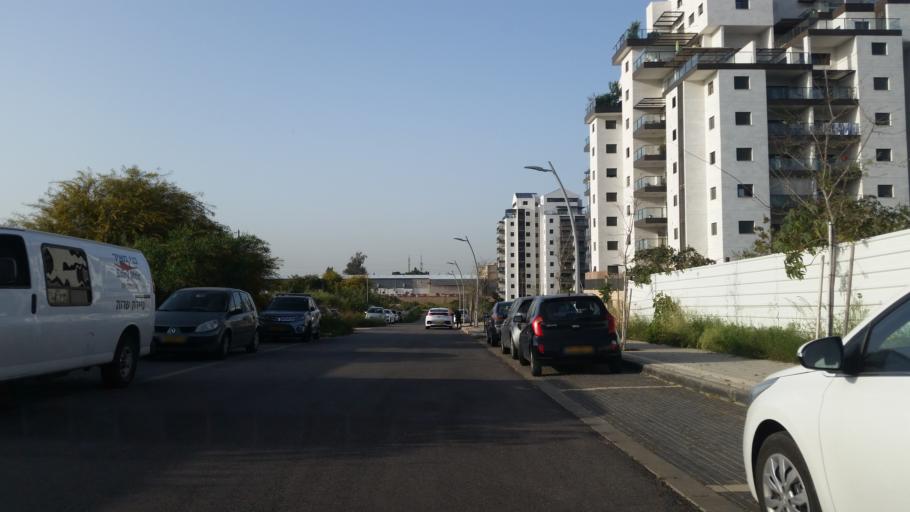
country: IL
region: Central District
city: Ra'anana
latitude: 32.1952
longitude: 34.8884
